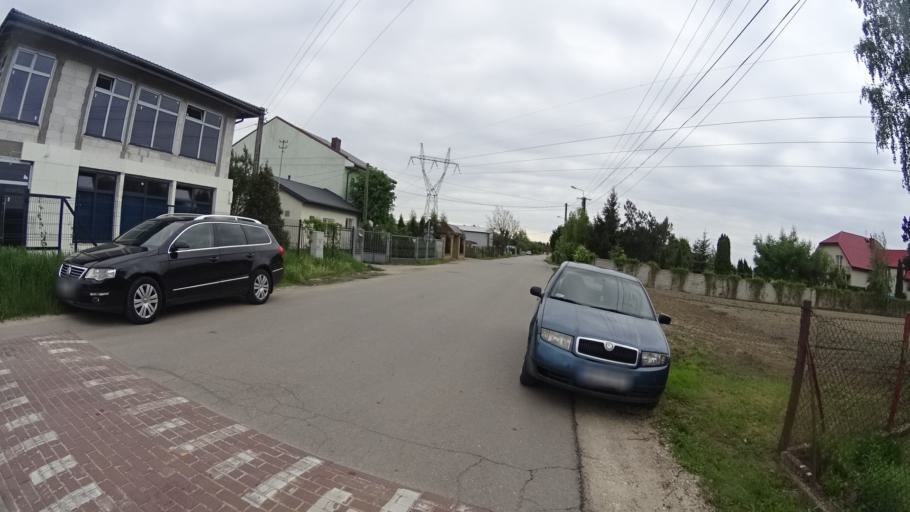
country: PL
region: Masovian Voivodeship
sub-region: Powiat warszawski zachodni
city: Stare Babice
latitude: 52.2431
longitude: 20.8316
